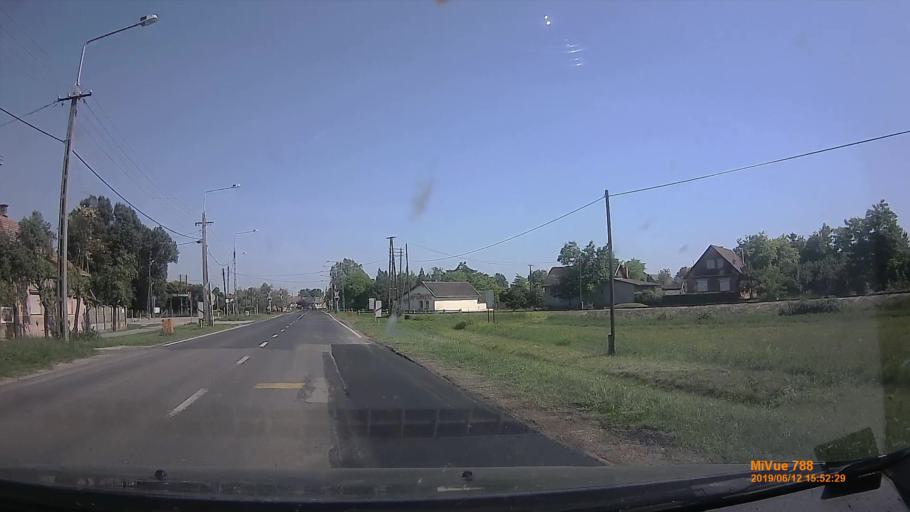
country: HU
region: Csongrad
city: Apatfalva
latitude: 46.1770
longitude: 20.5752
